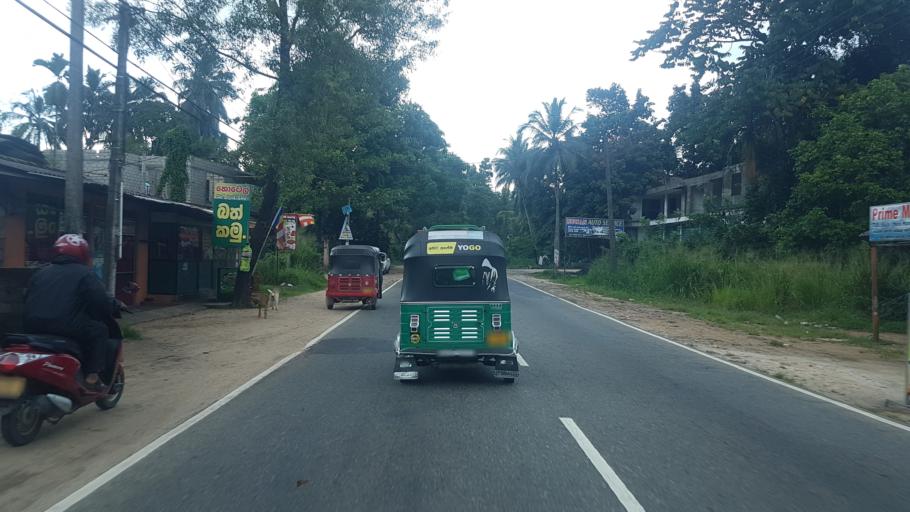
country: LK
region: Western
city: Hanwella Ihala
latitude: 7.0089
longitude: 80.2617
